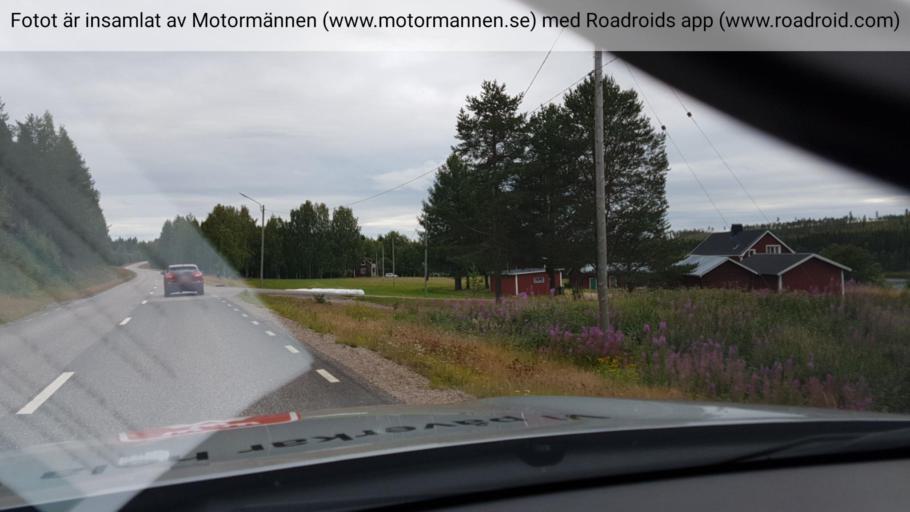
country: SE
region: Norrbotten
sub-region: Overkalix Kommun
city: OEverkalix
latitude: 66.5384
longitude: 22.7543
